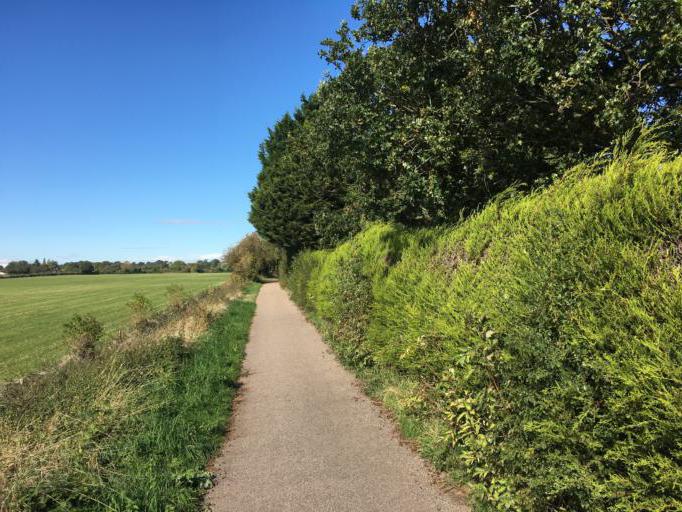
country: GB
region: England
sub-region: Warwickshire
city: Kenilworth
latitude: 52.3681
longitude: -1.5847
